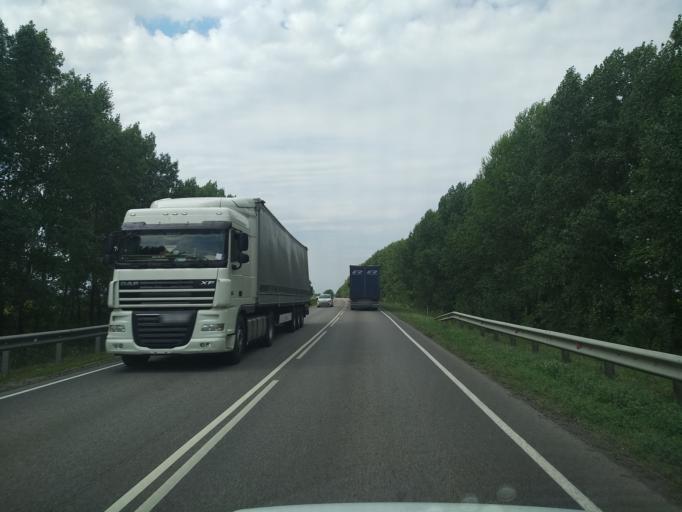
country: RU
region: Voronezj
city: Pereleshinskiy
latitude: 51.8477
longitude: 40.3130
